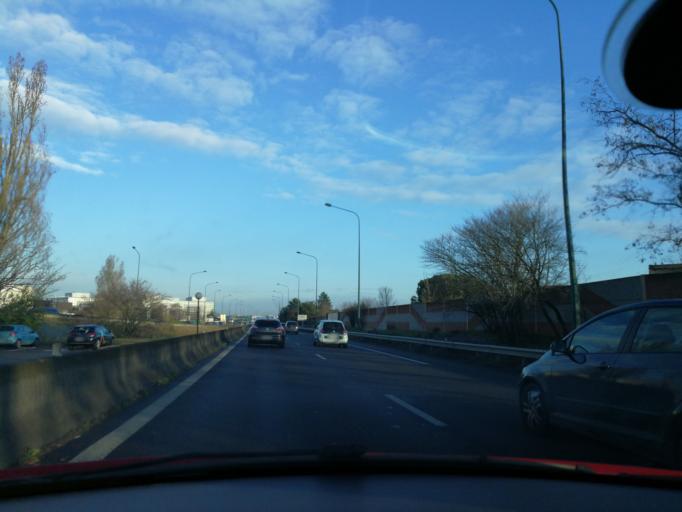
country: FR
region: Midi-Pyrenees
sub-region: Departement de la Haute-Garonne
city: Blagnac
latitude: 43.6338
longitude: 1.3799
